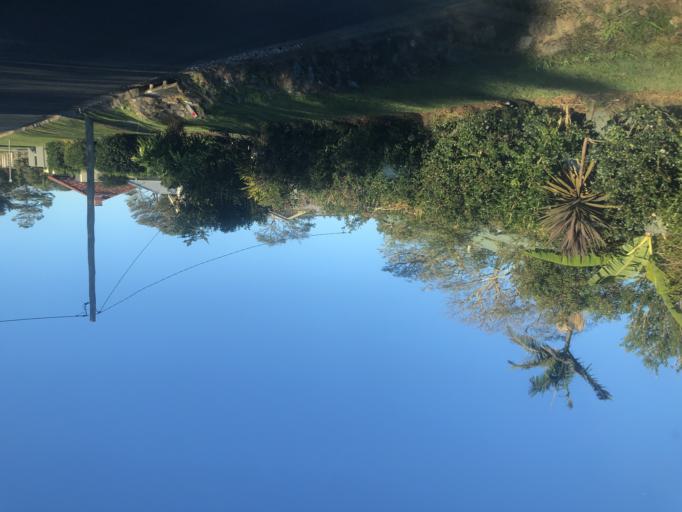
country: AU
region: New South Wales
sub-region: Coffs Harbour
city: Coffs Harbour
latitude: -30.3083
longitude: 153.1298
